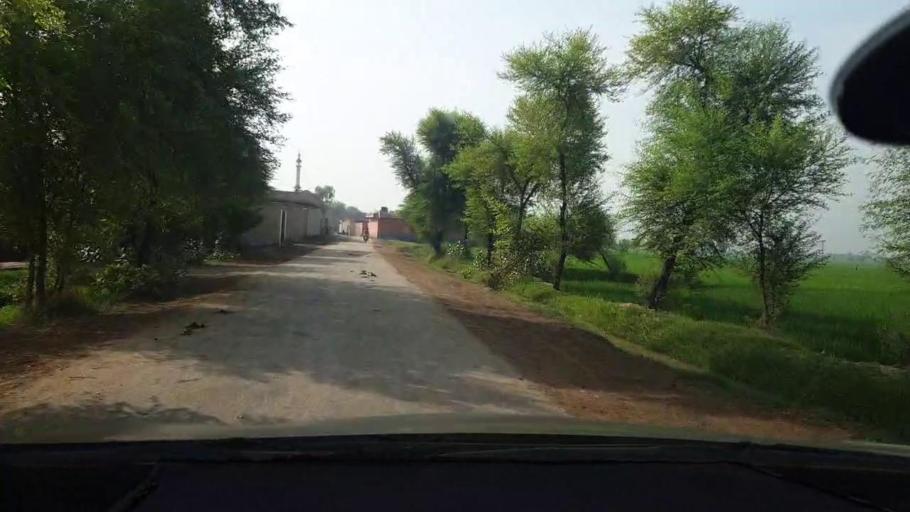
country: PK
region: Sindh
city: Goth Garelo
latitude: 27.4892
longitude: 68.0107
